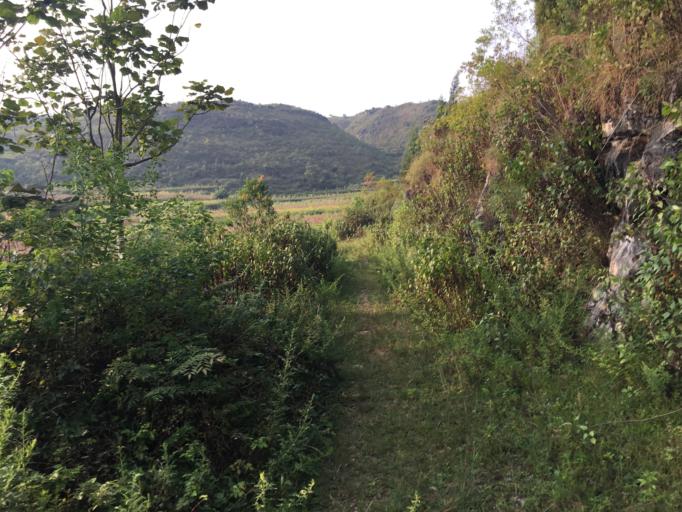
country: CN
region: Guangxi Zhuangzu Zizhiqu
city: Xinzhou
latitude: 25.4408
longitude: 105.6363
